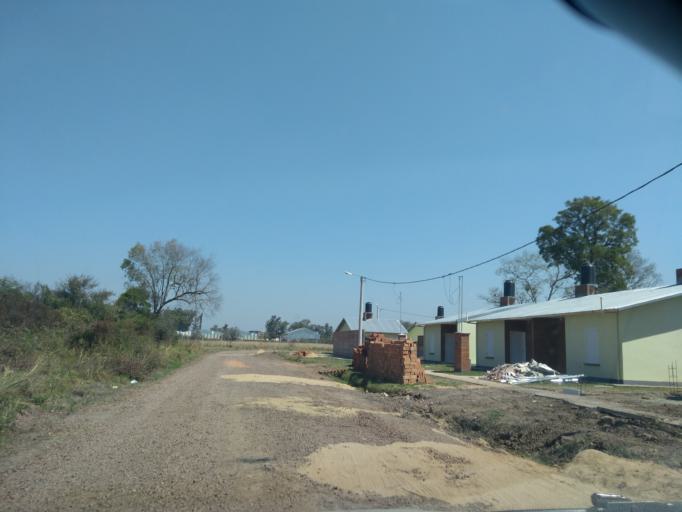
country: AR
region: Chaco
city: Fontana
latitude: -27.4085
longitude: -58.9727
